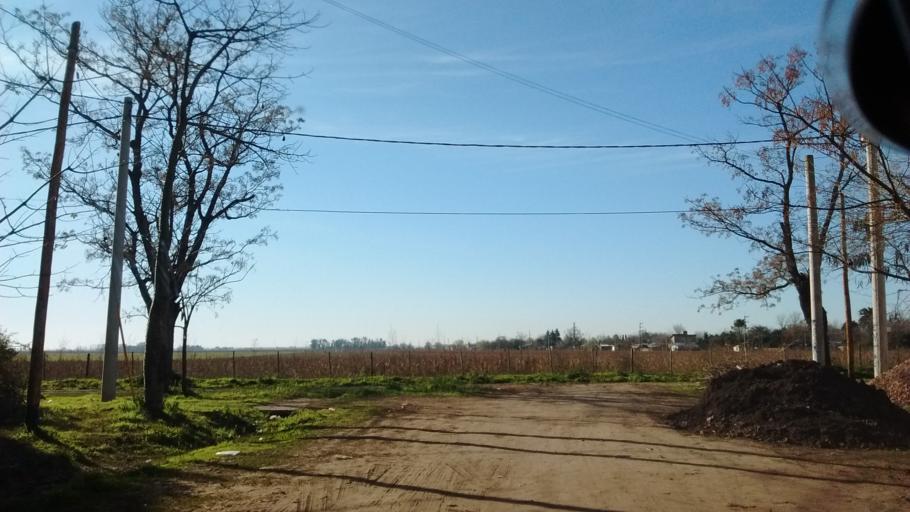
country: AR
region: Santa Fe
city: Funes
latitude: -32.9113
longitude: -60.8175
